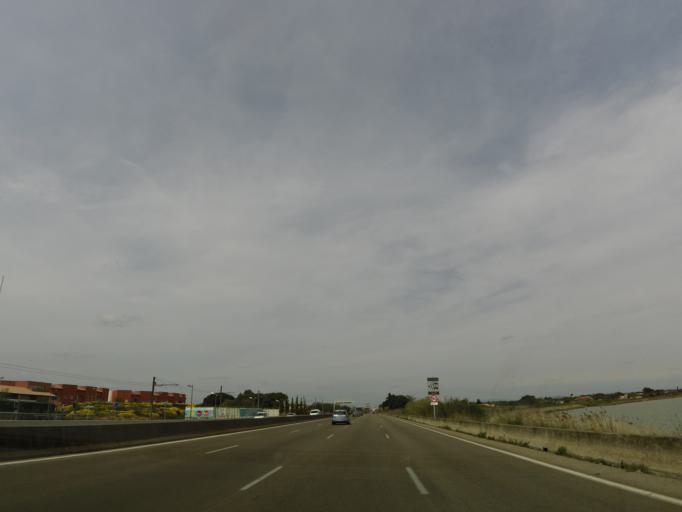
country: FR
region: Languedoc-Roussillon
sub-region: Departement de l'Herault
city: Perols
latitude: 43.5579
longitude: 3.9642
